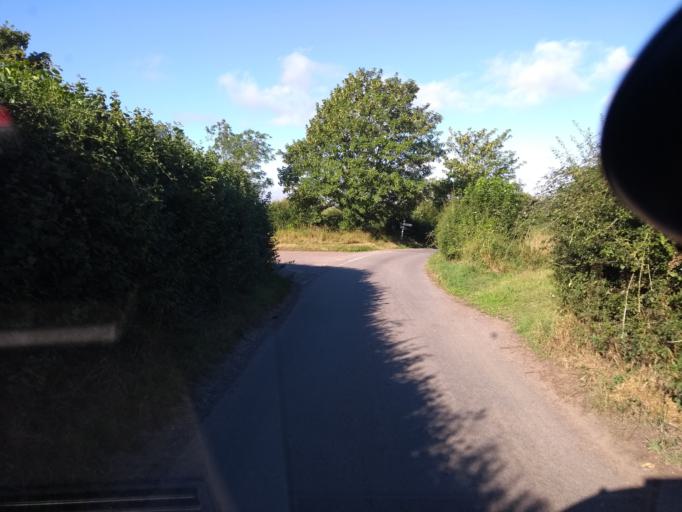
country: GB
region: England
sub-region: Somerset
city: Ilminster
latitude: 50.9251
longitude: -2.8670
